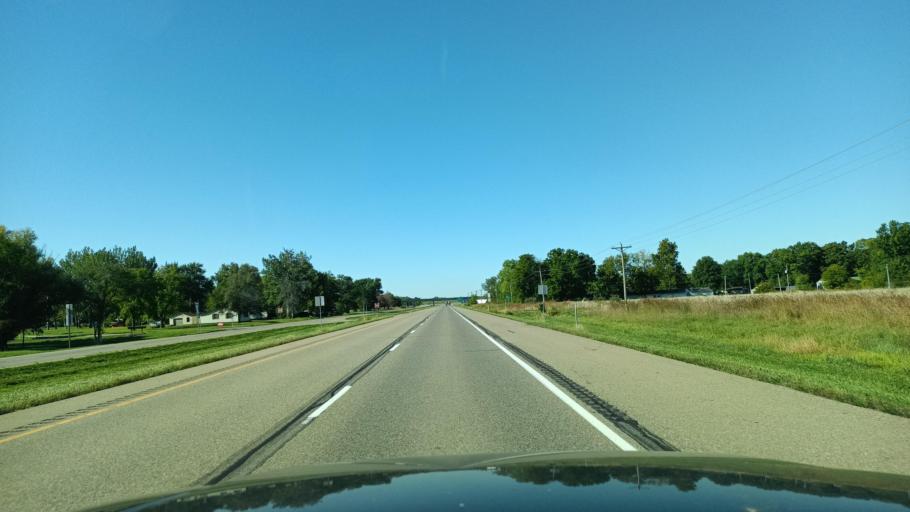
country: US
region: Iowa
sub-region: Lee County
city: Fort Madison
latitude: 40.6774
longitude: -91.2575
